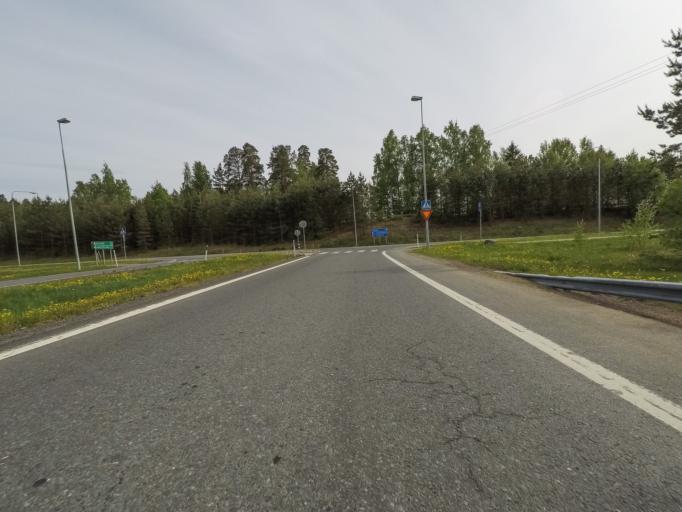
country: FI
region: Pirkanmaa
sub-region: Etelae-Pirkanmaa
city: Akaa
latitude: 61.1609
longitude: 23.9588
